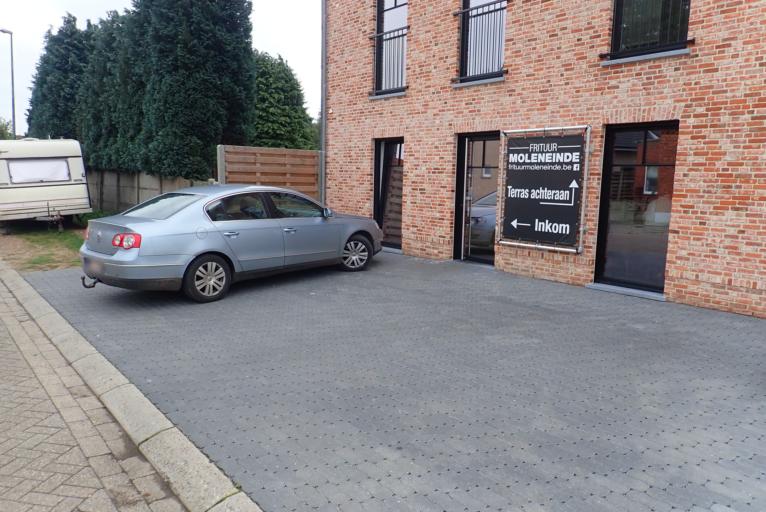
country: BE
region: Flanders
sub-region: Provincie Antwerpen
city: Vorselaar
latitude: 51.2070
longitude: 4.7626
